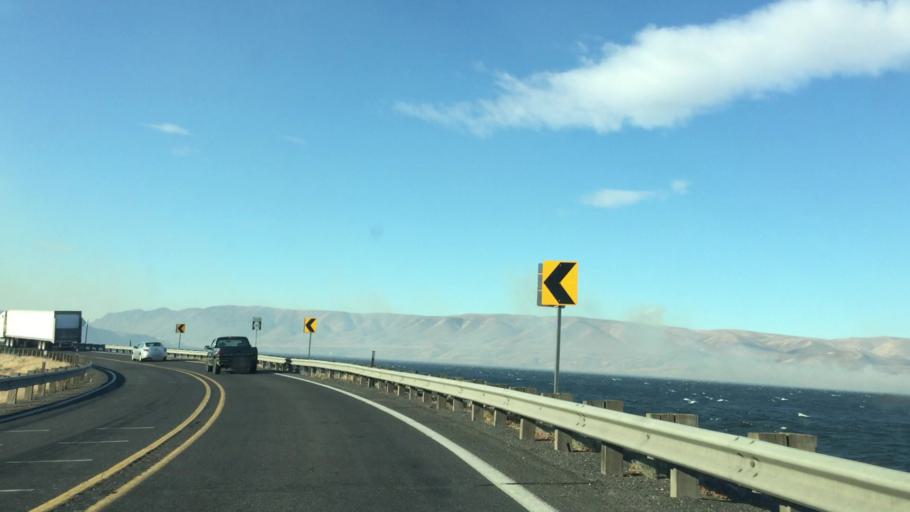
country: US
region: Washington
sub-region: Grant County
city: Mattawa
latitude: 46.9303
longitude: -119.9574
